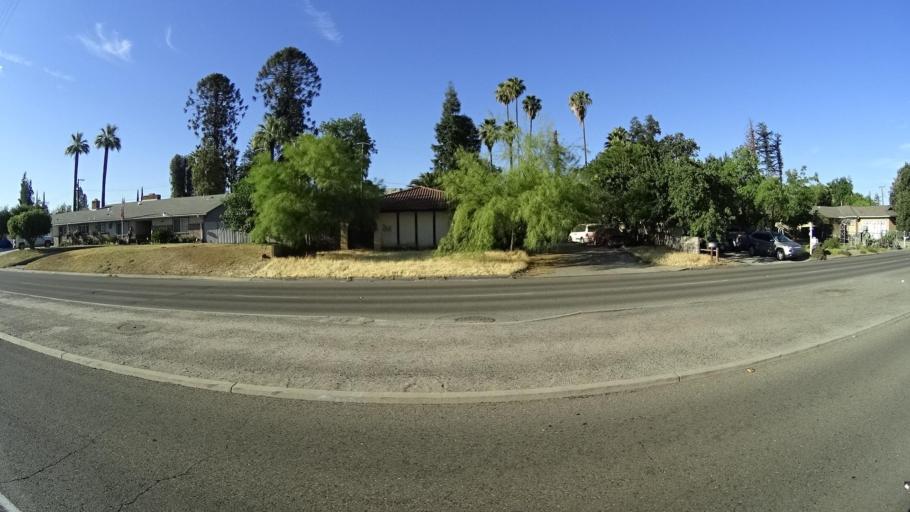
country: US
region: California
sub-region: Fresno County
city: Sunnyside
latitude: 36.7507
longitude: -119.7070
